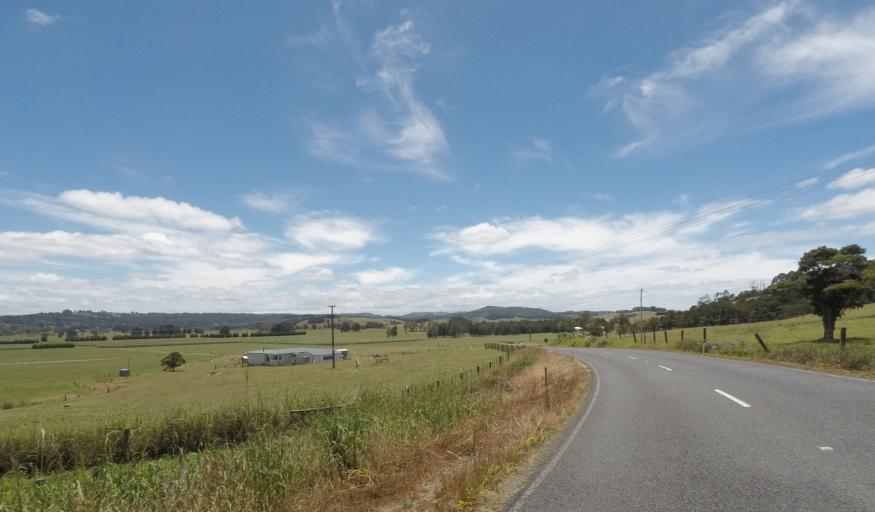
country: NZ
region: Northland
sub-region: Whangarei
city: Whangarei
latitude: -35.5592
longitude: 174.2917
